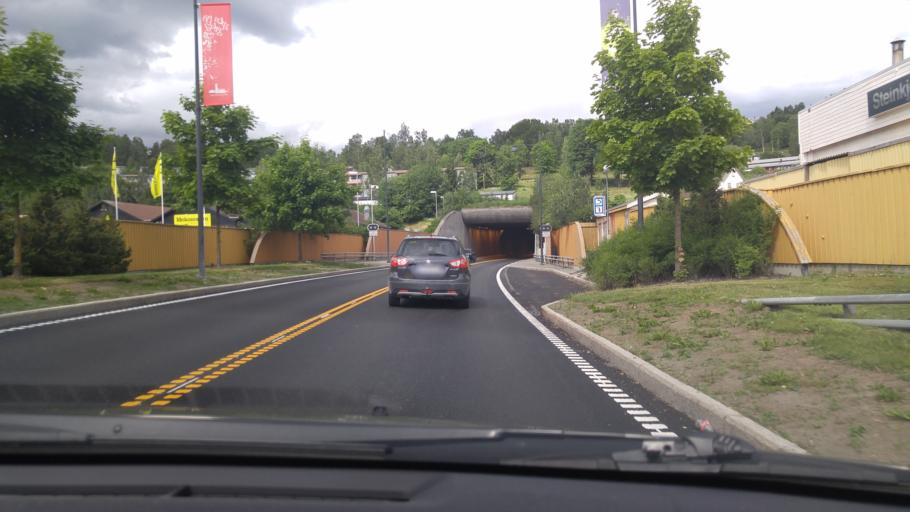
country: NO
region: Nord-Trondelag
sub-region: Steinkjer
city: Steinkjer
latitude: 64.0228
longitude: 11.4877
